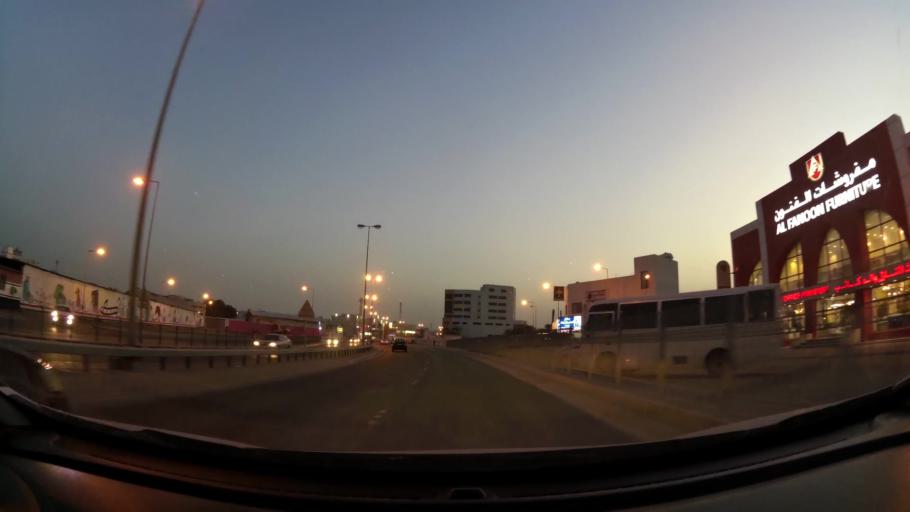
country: BH
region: Manama
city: Jidd Hafs
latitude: 26.2112
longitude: 50.5549
